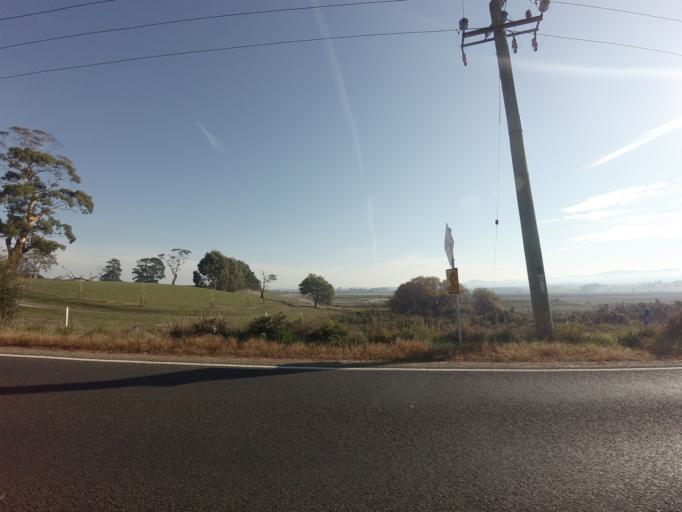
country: AU
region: Tasmania
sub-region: Launceston
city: Summerhill
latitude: -41.5286
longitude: 147.0180
